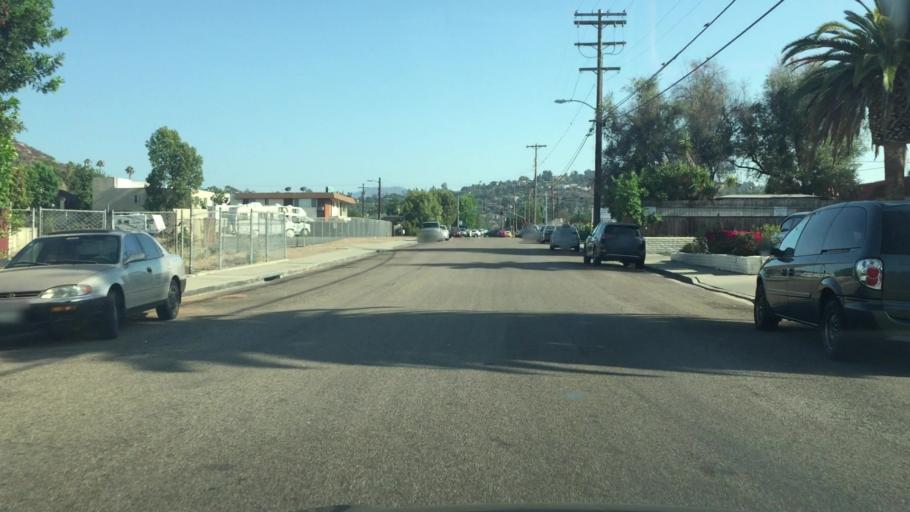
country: US
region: California
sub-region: San Diego County
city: El Cajon
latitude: 32.7896
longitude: -116.9482
